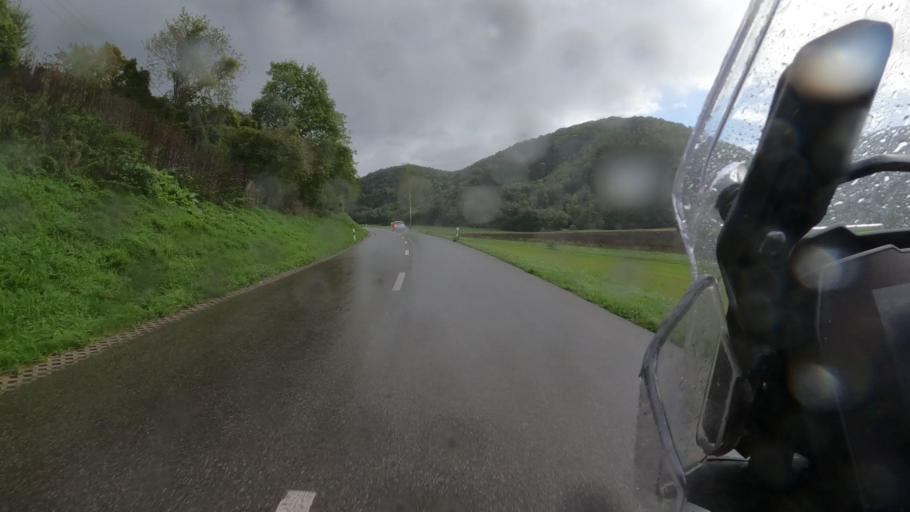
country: CH
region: Schaffhausen
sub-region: Bezirk Unterklettgau
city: Wilchingen
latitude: 47.6531
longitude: 8.4881
